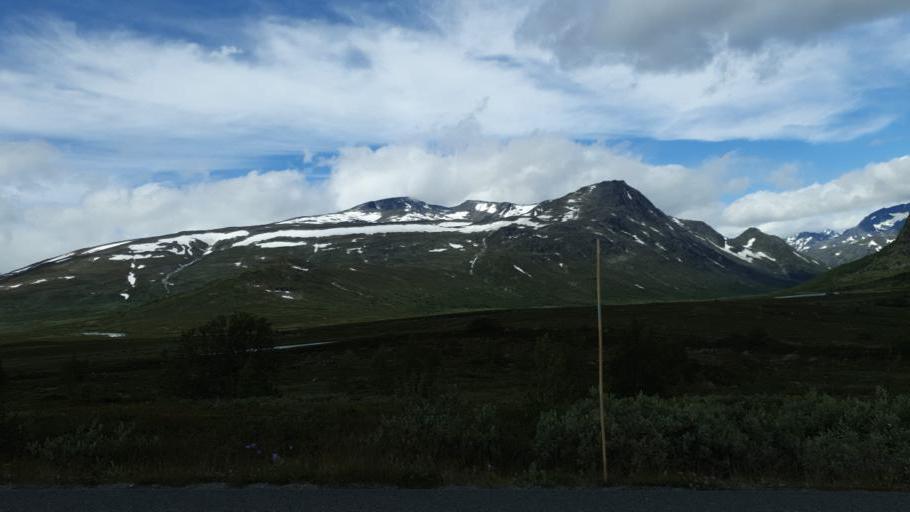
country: NO
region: Oppland
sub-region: Vang
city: Vang
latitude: 61.4607
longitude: 8.8064
